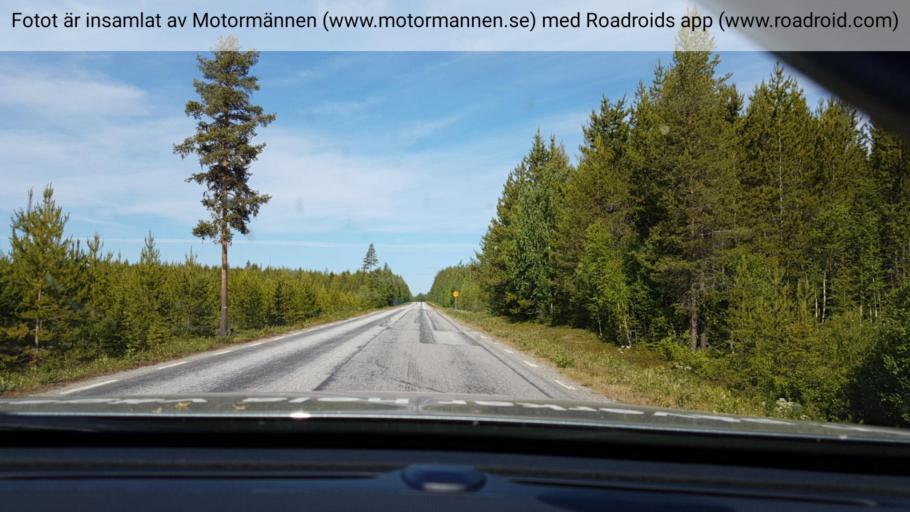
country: SE
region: Vaesterbotten
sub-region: Dorotea Kommun
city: Dorotea
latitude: 64.3687
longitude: 16.1397
